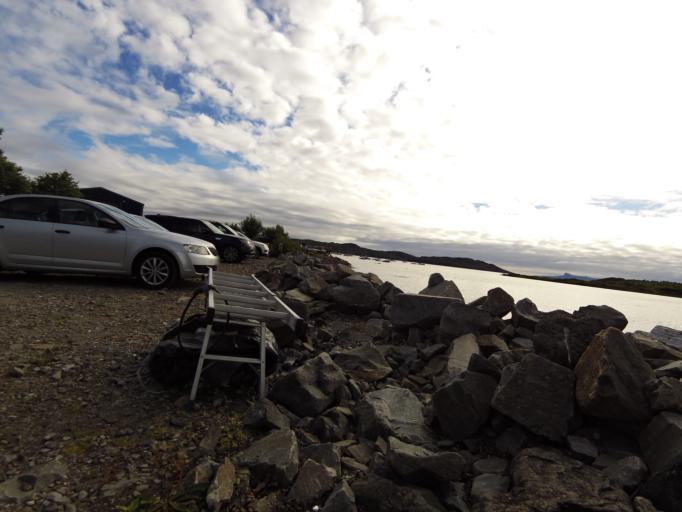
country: GB
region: Scotland
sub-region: Argyll and Bute
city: Isle Of Mull
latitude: 56.9109
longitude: -5.8492
